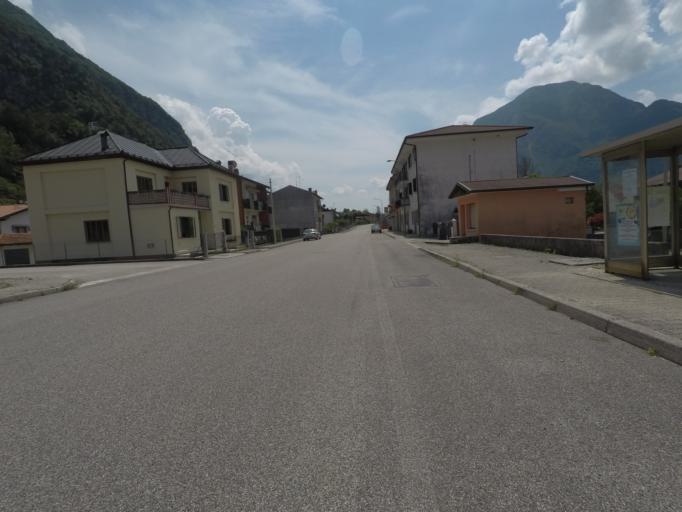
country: IT
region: Friuli Venezia Giulia
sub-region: Provincia di Udine
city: Amaro
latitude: 46.3733
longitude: 13.1347
